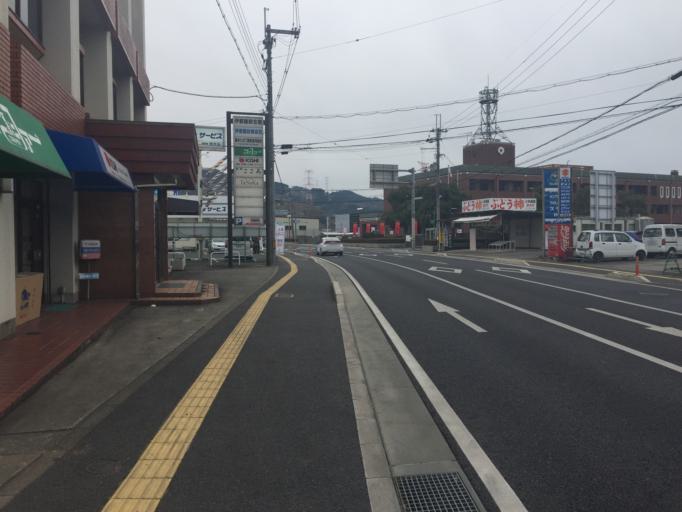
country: JP
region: Wakayama
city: Hashimoto
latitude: 34.3126
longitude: 135.6018
